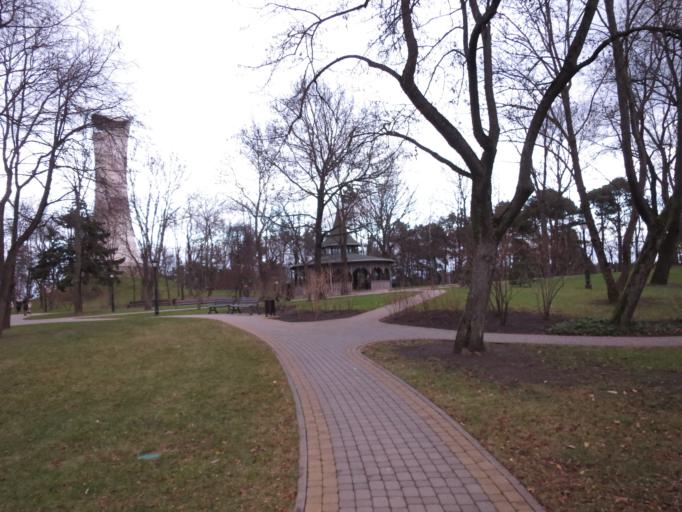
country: LV
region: Riga
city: Bolderaja
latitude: 57.0363
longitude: 24.1030
